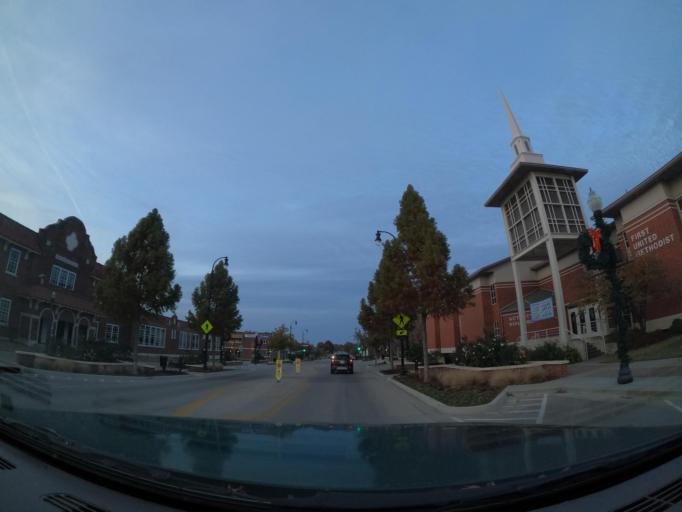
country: US
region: Oklahoma
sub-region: Tulsa County
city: Broken Arrow
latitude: 36.0538
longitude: -95.7908
